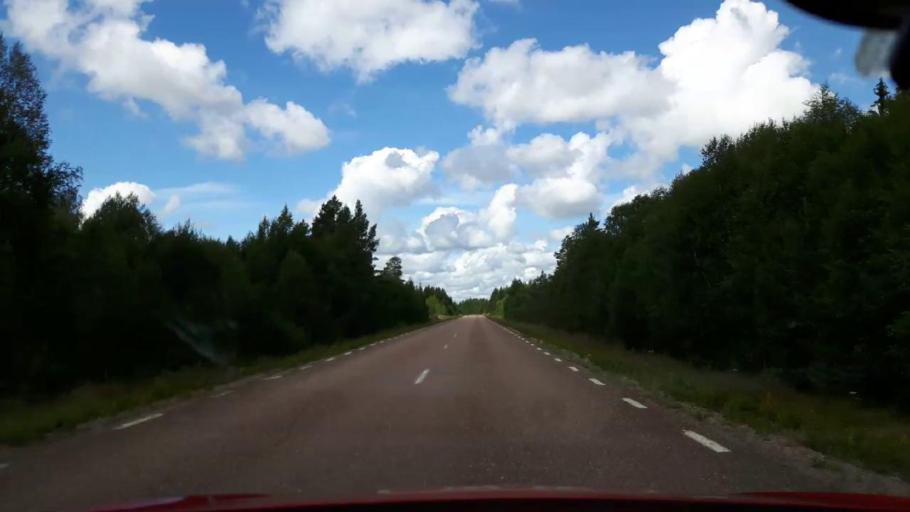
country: SE
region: Dalarna
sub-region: Alvdalens Kommun
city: AElvdalen
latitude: 61.8020
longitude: 13.6630
